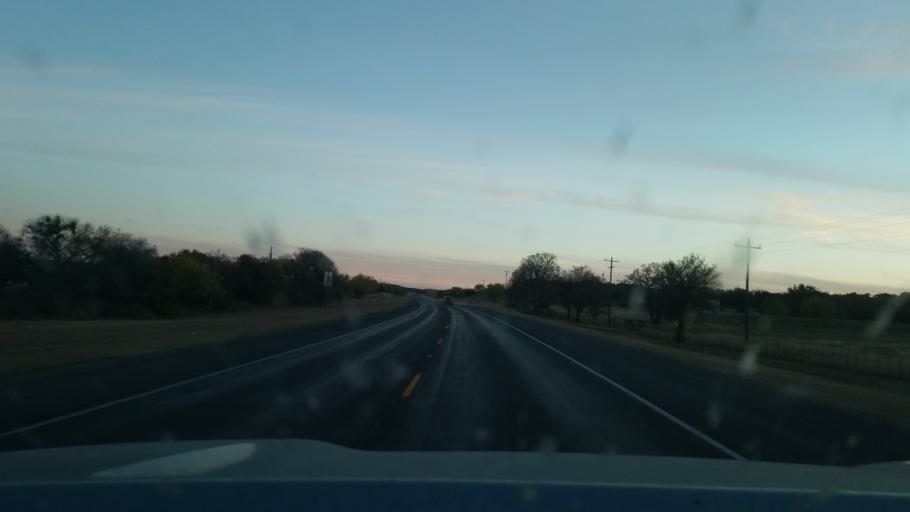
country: US
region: Texas
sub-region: Stephens County
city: Breckenridge
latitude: 32.5973
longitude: -98.8994
